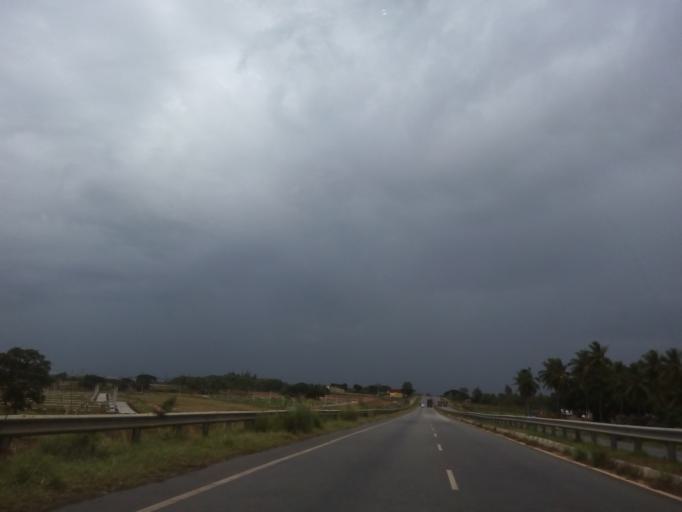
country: IN
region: Karnataka
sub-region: Davanagere
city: Harihar
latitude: 14.4579
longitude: 75.8615
